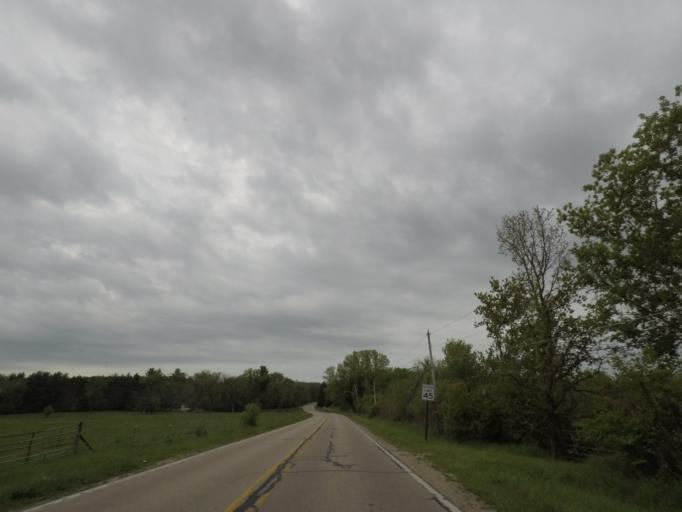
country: US
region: Illinois
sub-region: Winnebago County
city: Roscoe
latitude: 42.4155
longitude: -88.9776
